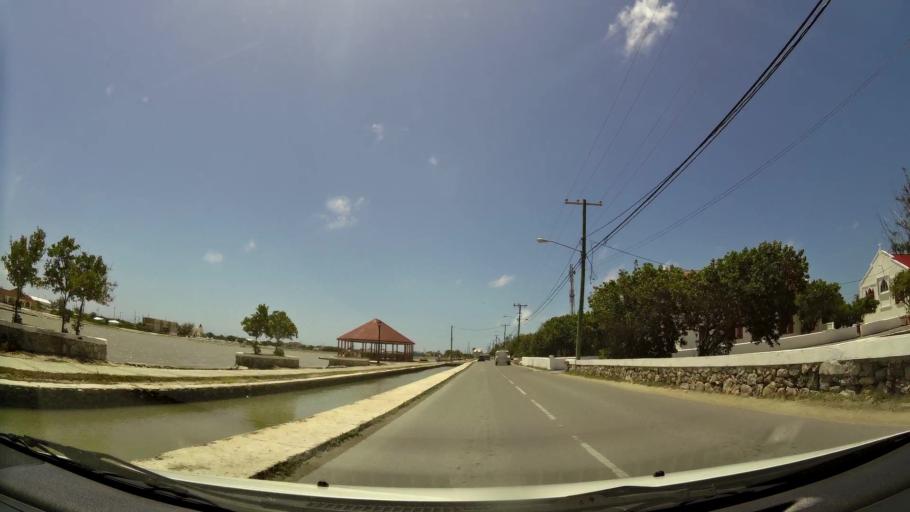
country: TC
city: Cockburn Town
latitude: 21.4679
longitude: -71.1458
